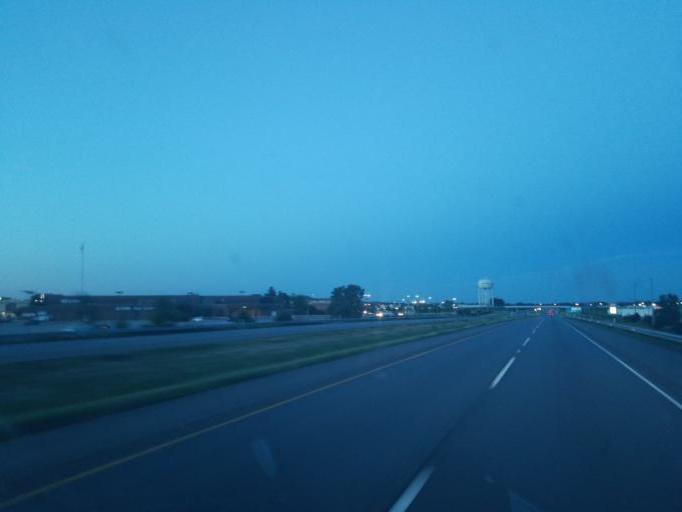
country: US
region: Indiana
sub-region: Saint Joseph County
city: Georgetown
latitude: 41.7161
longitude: -86.1949
